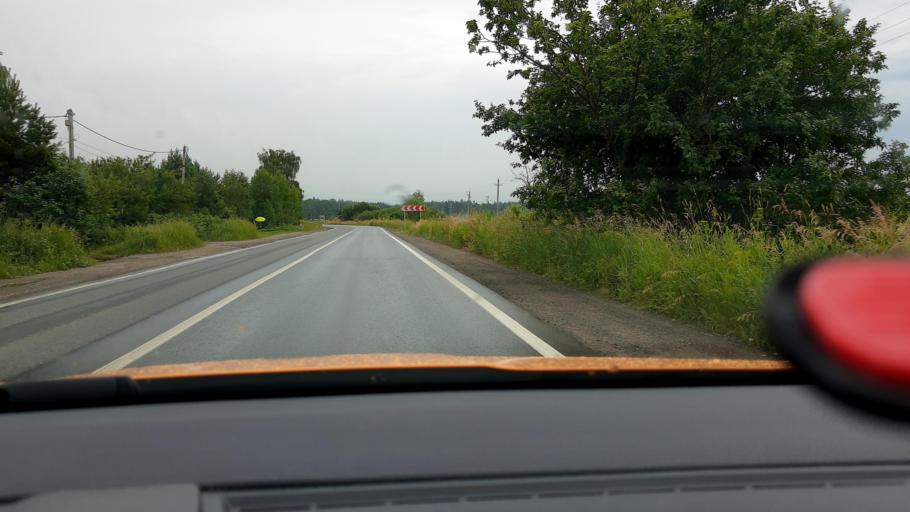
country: RU
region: Moskovskaya
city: Pirogovskiy
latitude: 55.9984
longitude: 37.7064
